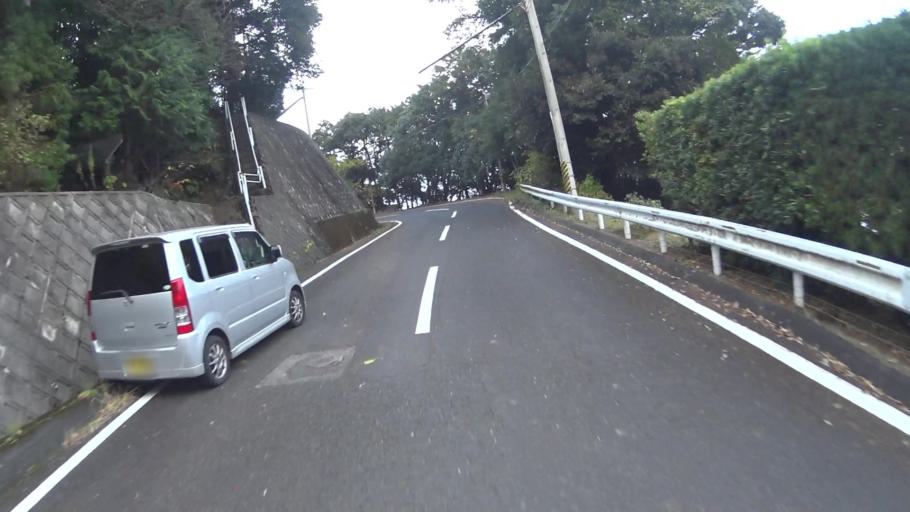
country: JP
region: Kyoto
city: Maizuru
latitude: 35.5668
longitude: 135.4526
